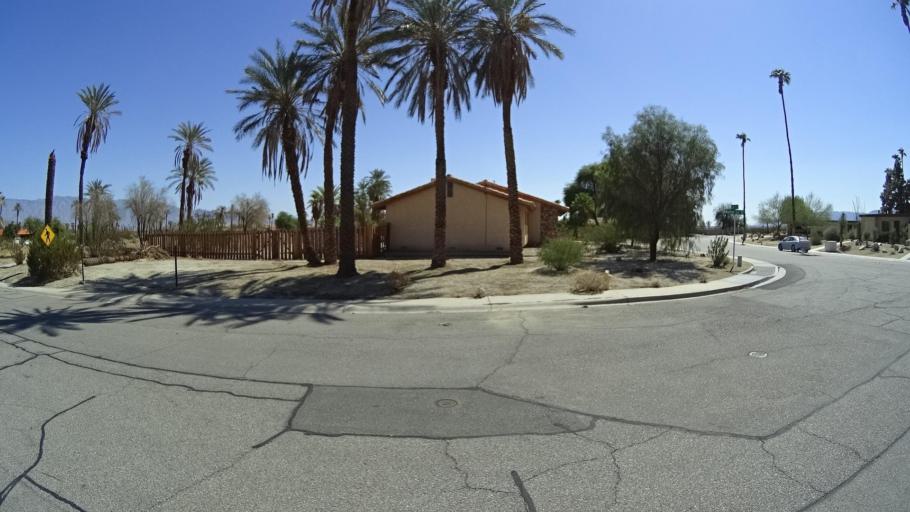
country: US
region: California
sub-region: San Diego County
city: Borrego Springs
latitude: 33.2344
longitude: -116.3568
